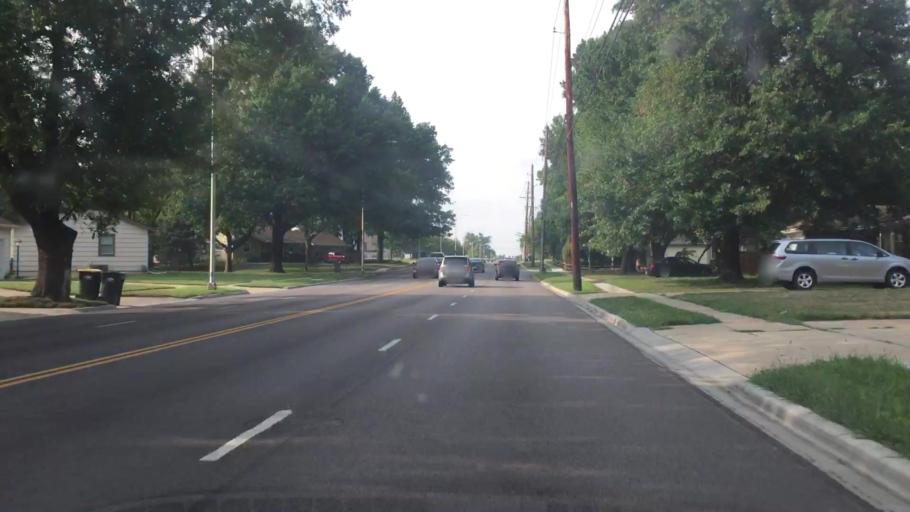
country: US
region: Kansas
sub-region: Johnson County
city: Overland Park
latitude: 38.9683
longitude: -94.6863
